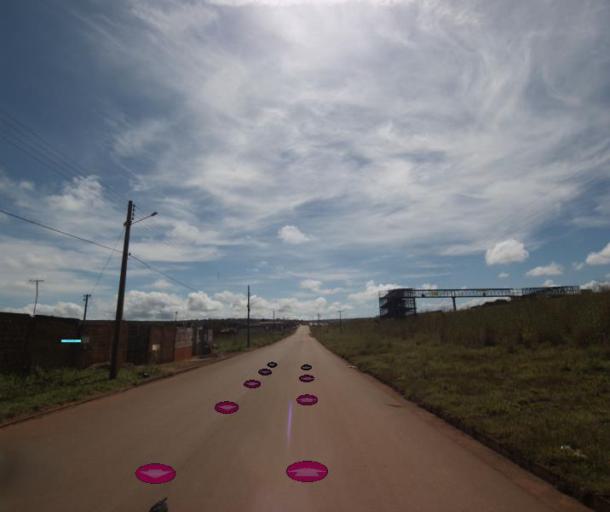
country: BR
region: Federal District
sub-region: Brasilia
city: Brasilia
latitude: -15.7536
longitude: -48.3281
